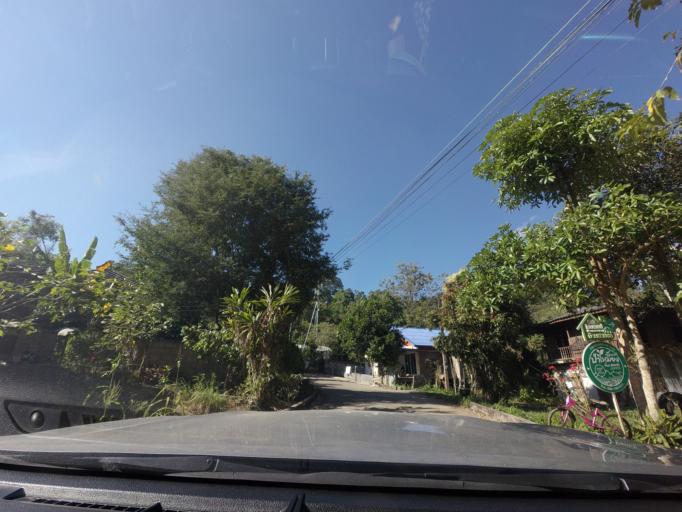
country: TH
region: Lampang
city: Mueang Pan
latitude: 18.8285
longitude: 99.3849
